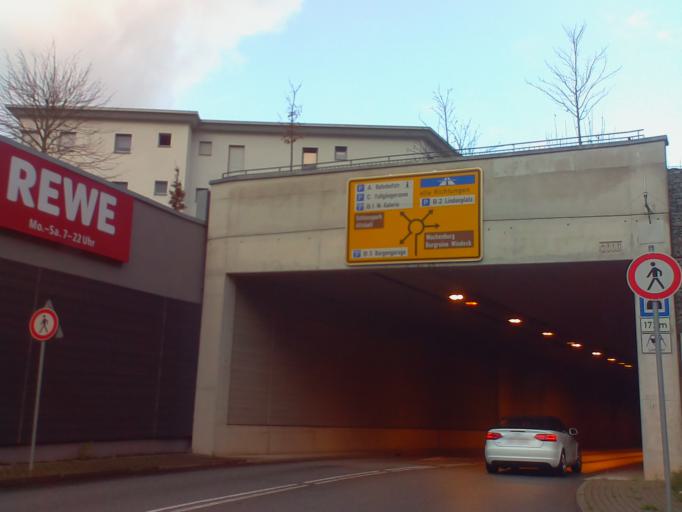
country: DE
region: Baden-Wuerttemberg
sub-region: Karlsruhe Region
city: Weinheim
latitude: 49.5473
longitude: 8.6744
